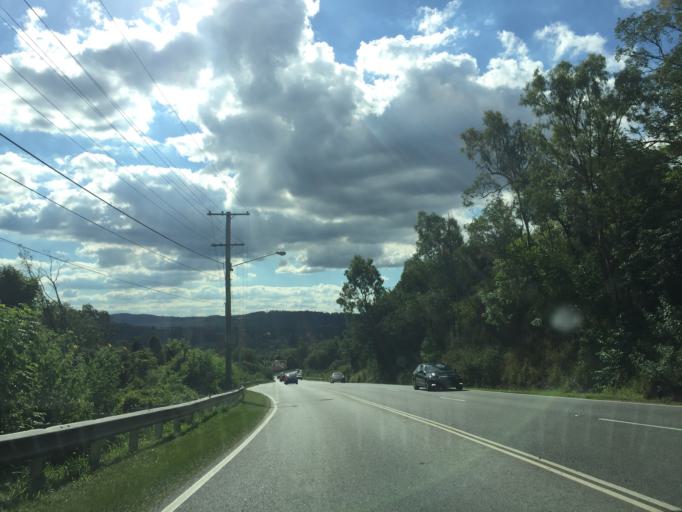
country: AU
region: Queensland
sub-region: Moreton Bay
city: Ferny Hills
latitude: -27.4241
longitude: 152.9490
